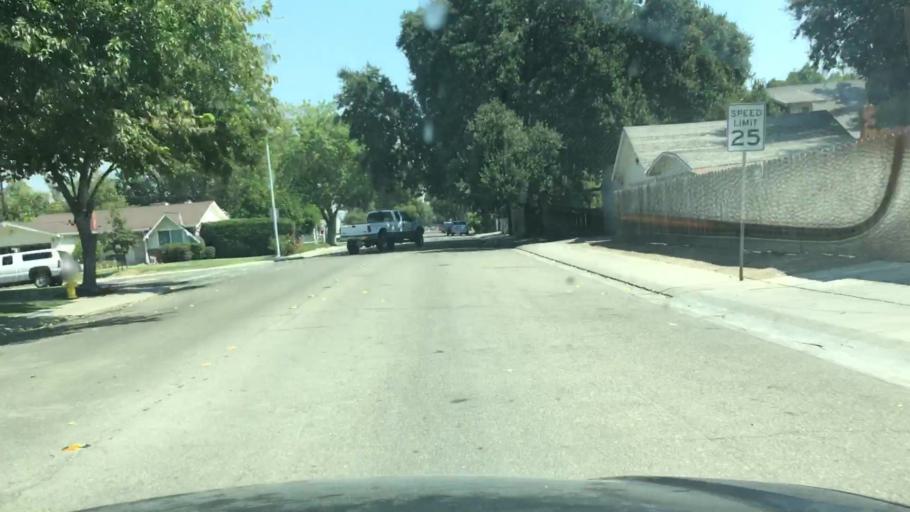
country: US
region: California
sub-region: San Joaquin County
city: Tracy
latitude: 37.7433
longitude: -121.4404
